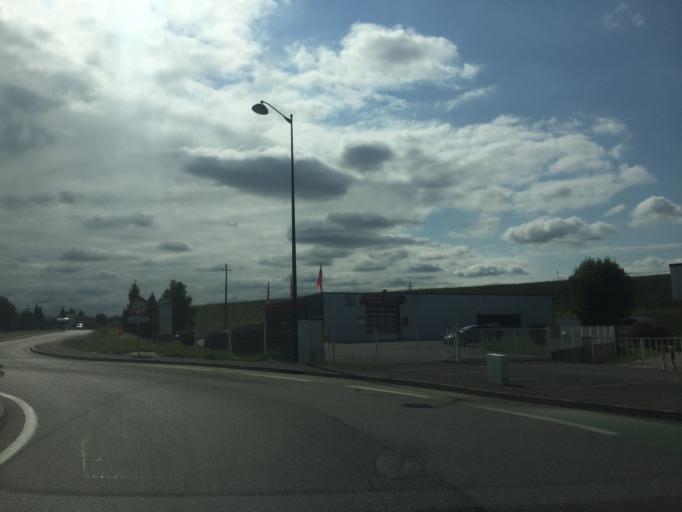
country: FR
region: Midi-Pyrenees
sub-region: Departement de la Haute-Garonne
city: Labarthe-Riviere
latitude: 43.0962
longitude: 0.7025
